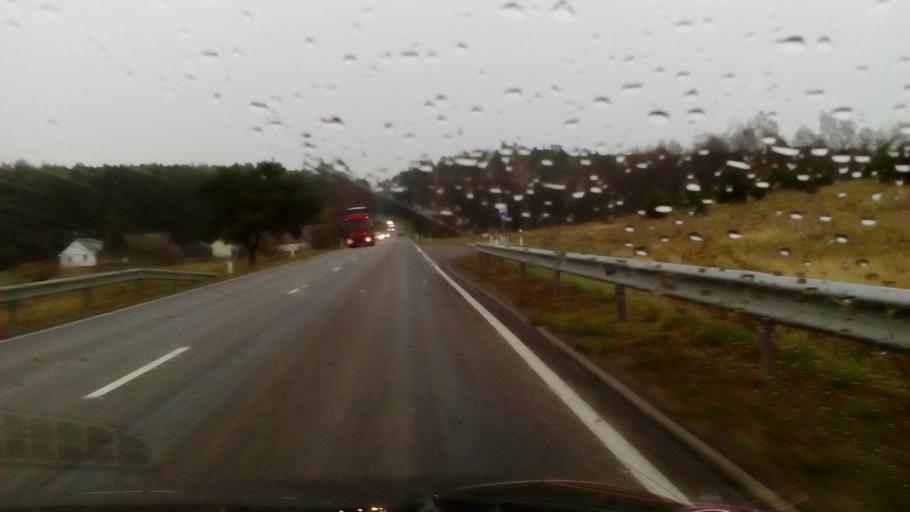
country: LT
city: Prienai
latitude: 54.5967
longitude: 23.8455
